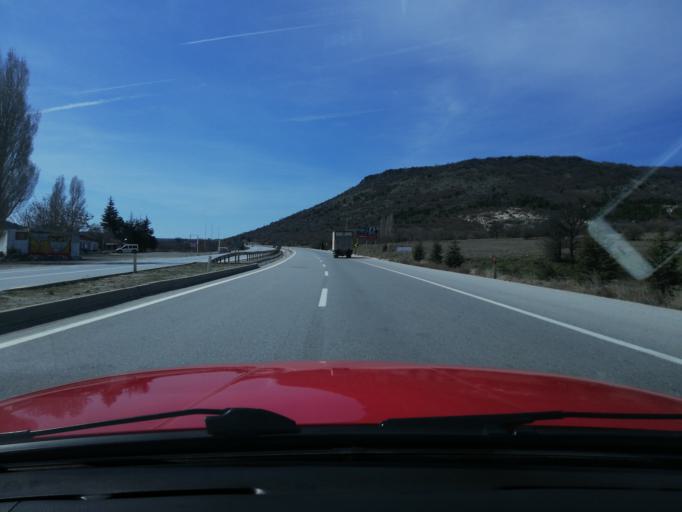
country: TR
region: Kuetahya
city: Sabuncu
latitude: 39.6057
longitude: 30.1482
